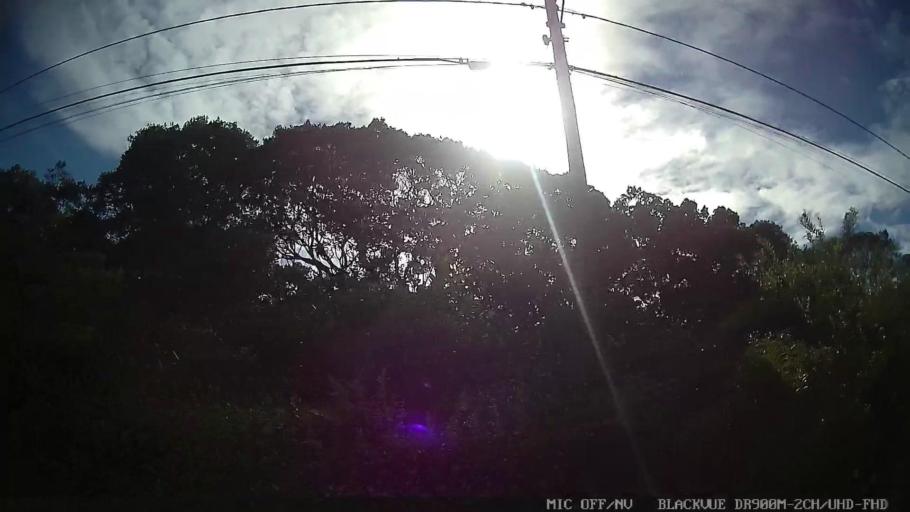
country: BR
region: Sao Paulo
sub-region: Peruibe
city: Peruibe
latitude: -24.2464
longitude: -46.9064
